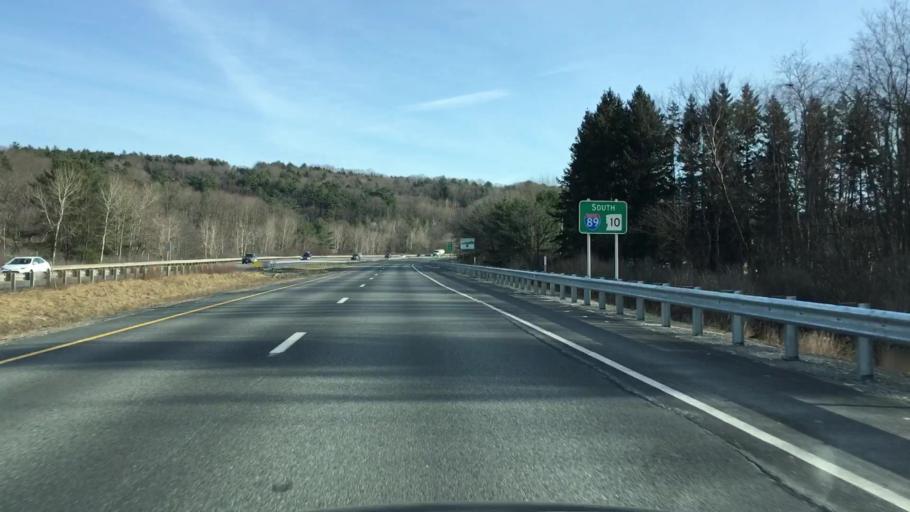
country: US
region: New Hampshire
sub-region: Grafton County
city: Lebanon
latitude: 43.6473
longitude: -72.2402
